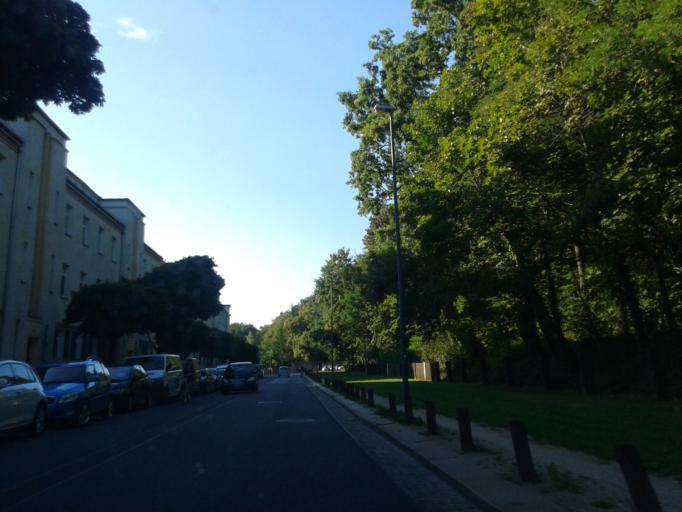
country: DE
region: Saxony
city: Albertstadt
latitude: 51.0835
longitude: 13.7439
